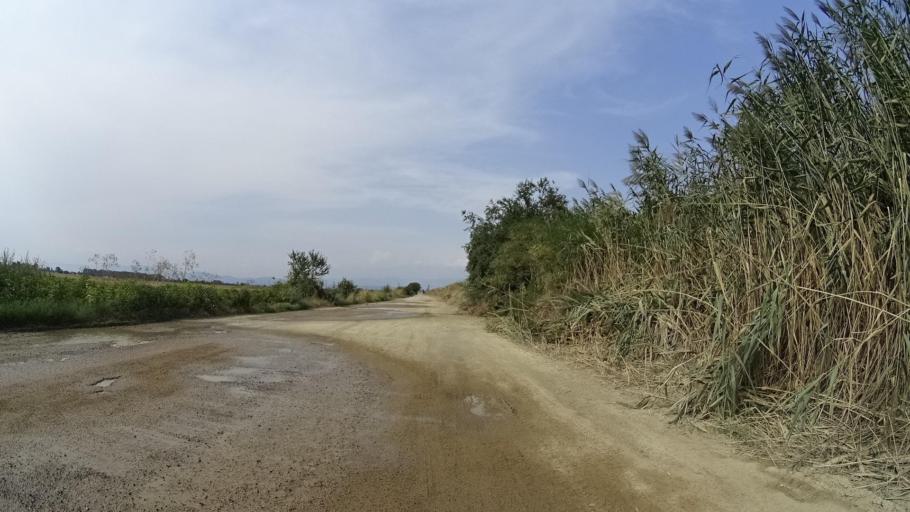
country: BG
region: Plovdiv
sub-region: Obshtina Kaloyanovo
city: Kaloyanovo
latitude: 42.3066
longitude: 24.7995
